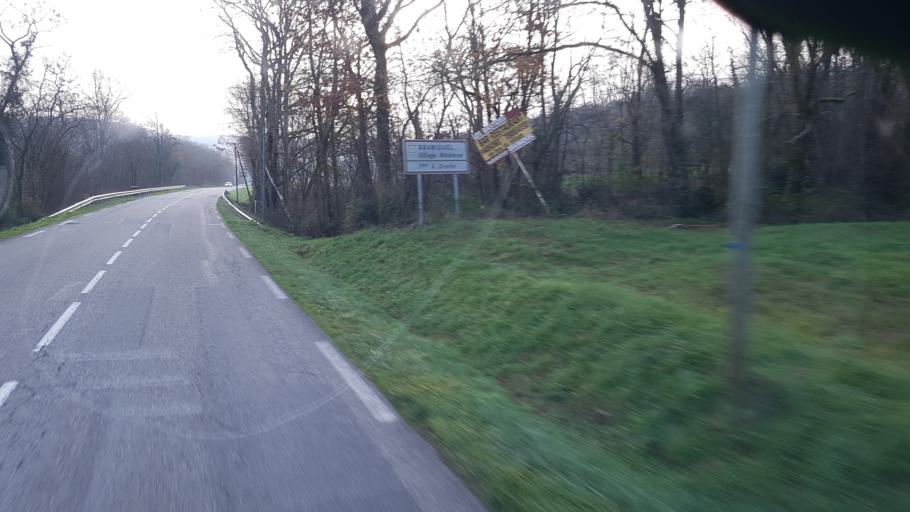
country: FR
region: Midi-Pyrenees
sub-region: Departement du Tarn-et-Garonne
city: Montricoux
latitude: 44.0724
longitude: 1.6461
